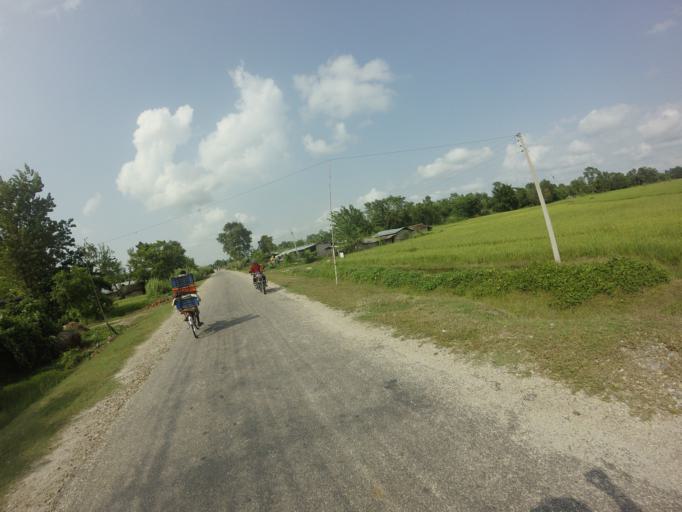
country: NP
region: Far Western
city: Tikapur
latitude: 28.4665
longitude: 81.0752
